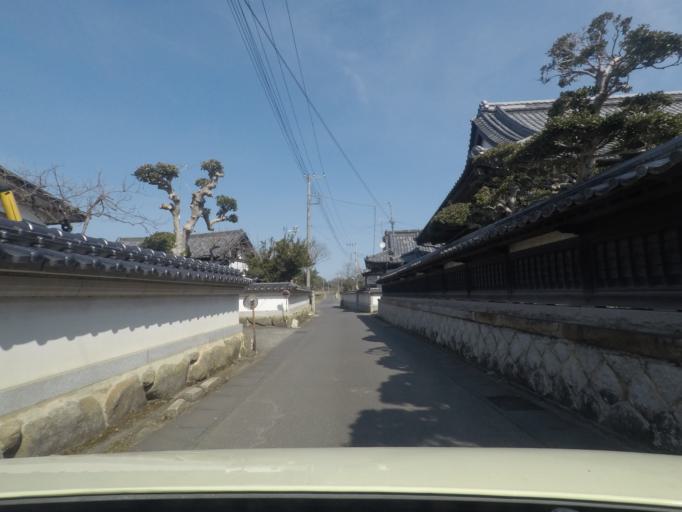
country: JP
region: Ibaraki
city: Ishioka
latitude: 36.1991
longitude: 140.3150
